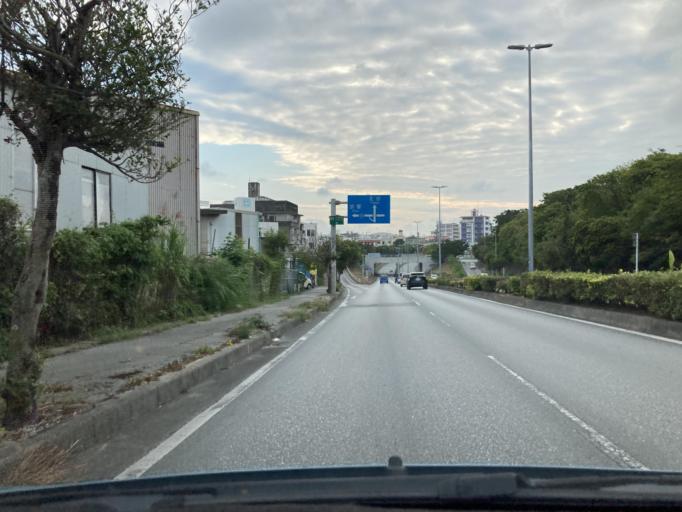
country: JP
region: Okinawa
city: Okinawa
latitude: 26.3394
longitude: 127.7970
